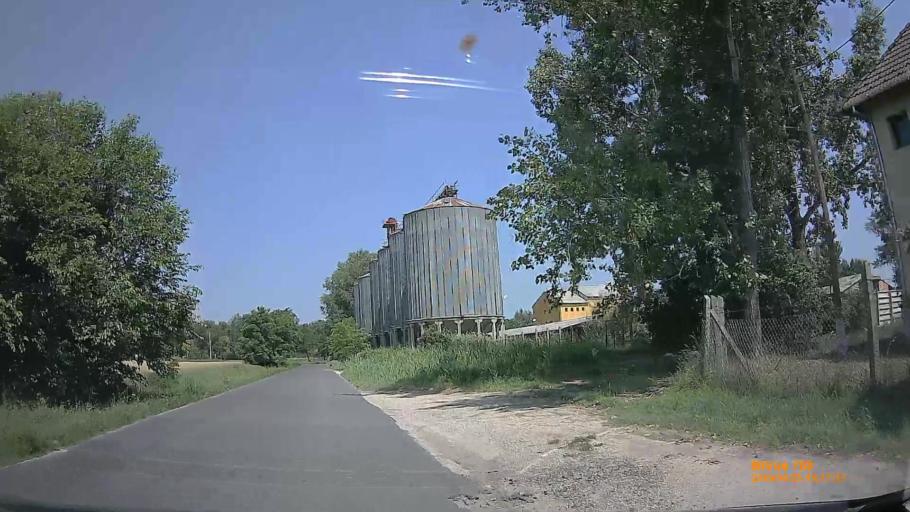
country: HU
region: Komarom-Esztergom
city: Tat
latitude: 47.7361
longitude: 18.6536
